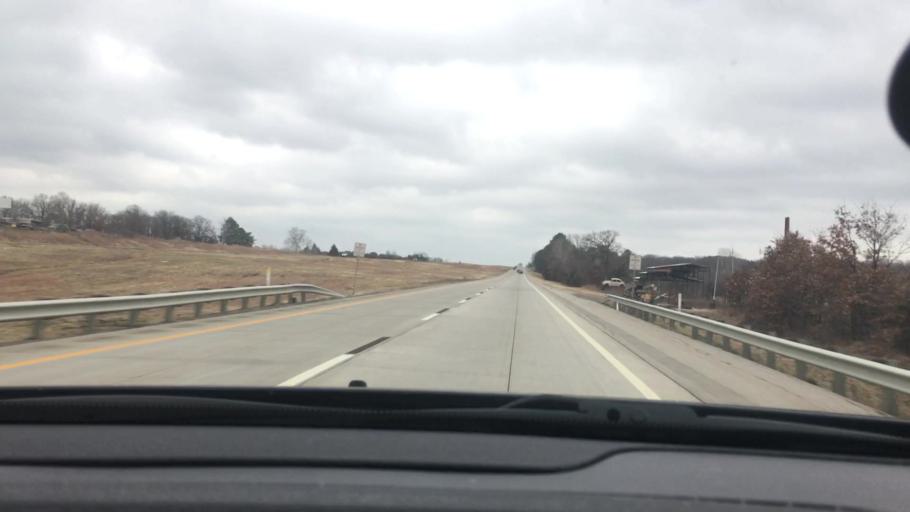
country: US
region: Oklahoma
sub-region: Bryan County
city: Durant
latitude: 34.1865
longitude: -96.2448
